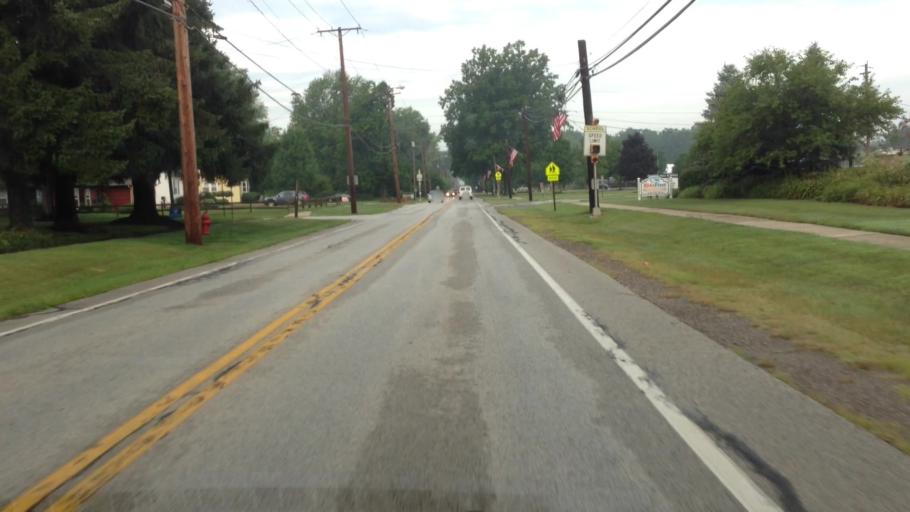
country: US
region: Ohio
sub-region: Cuyahoga County
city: Olmsted Falls
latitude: 41.3728
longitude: -81.9108
